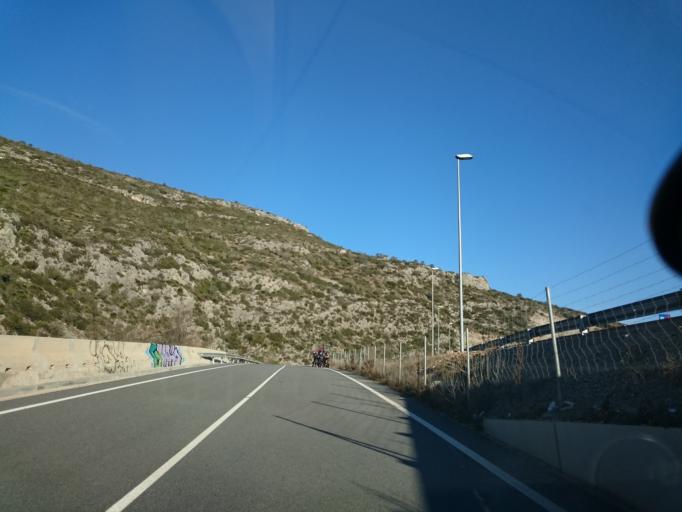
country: ES
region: Catalonia
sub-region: Provincia de Barcelona
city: Vilafranca del Penedes
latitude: 41.3055
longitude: 1.7214
